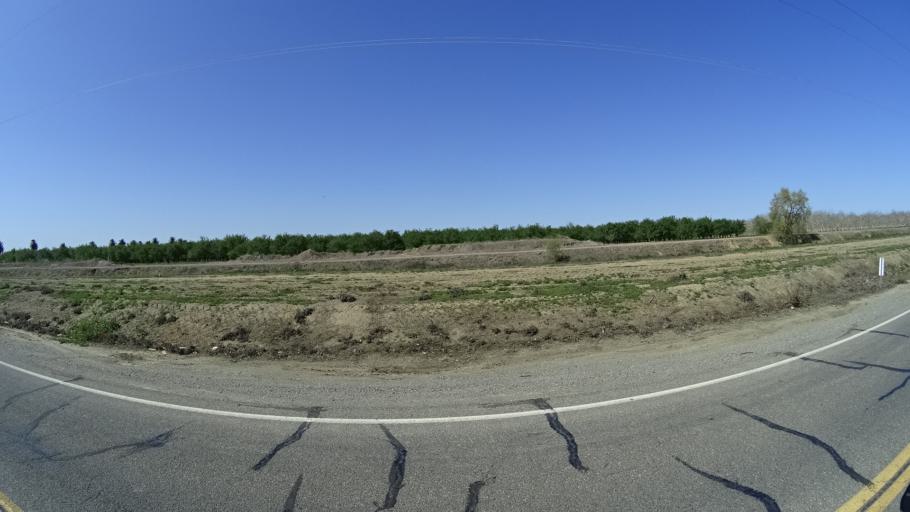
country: US
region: California
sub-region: Glenn County
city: Hamilton City
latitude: 39.7404
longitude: -122.0172
